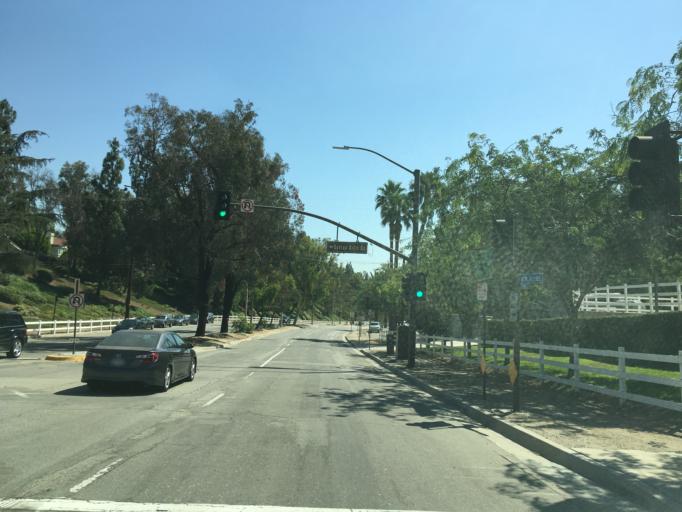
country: US
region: California
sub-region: Los Angeles County
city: Charter Oak
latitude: 34.0700
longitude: -117.8369
